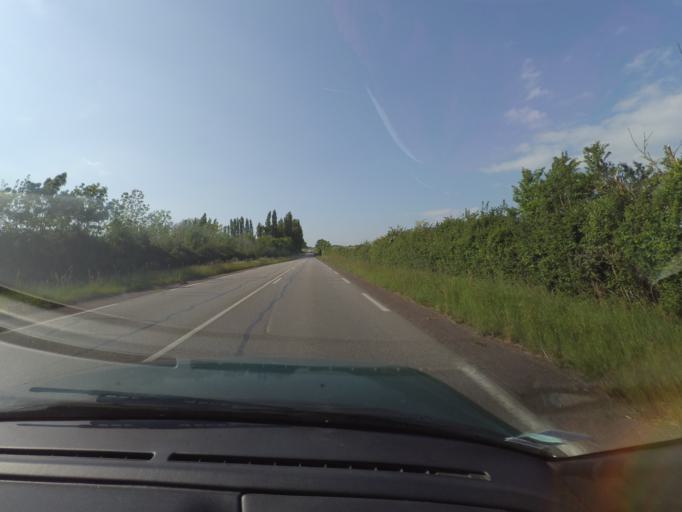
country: FR
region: Pays de la Loire
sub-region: Departement de la Vendee
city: Angles
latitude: 46.4441
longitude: -1.4083
